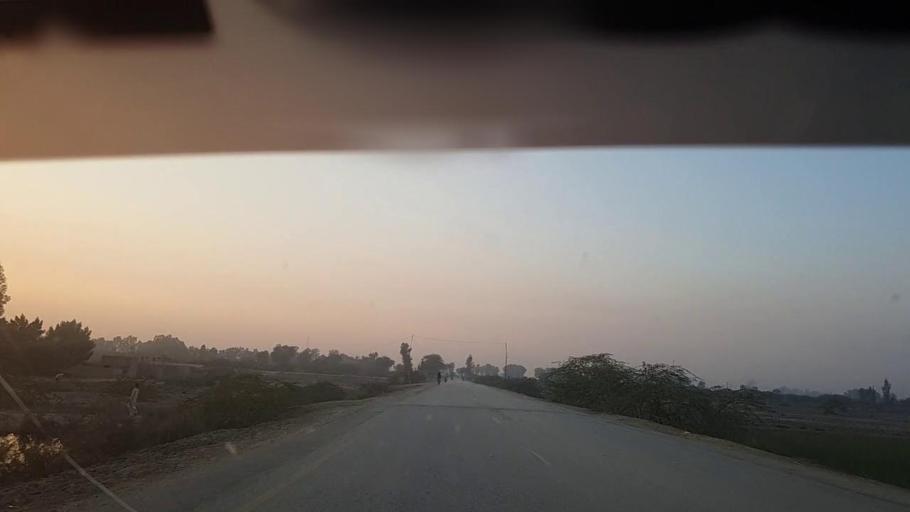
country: PK
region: Sindh
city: Ranipur
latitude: 27.2714
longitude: 68.5161
